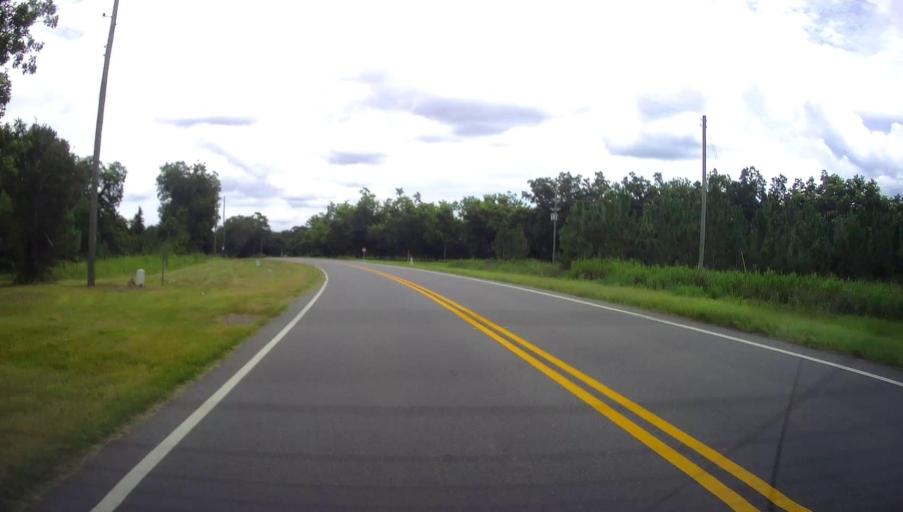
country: US
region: Georgia
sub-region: Macon County
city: Oglethorpe
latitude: 32.2643
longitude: -84.0979
